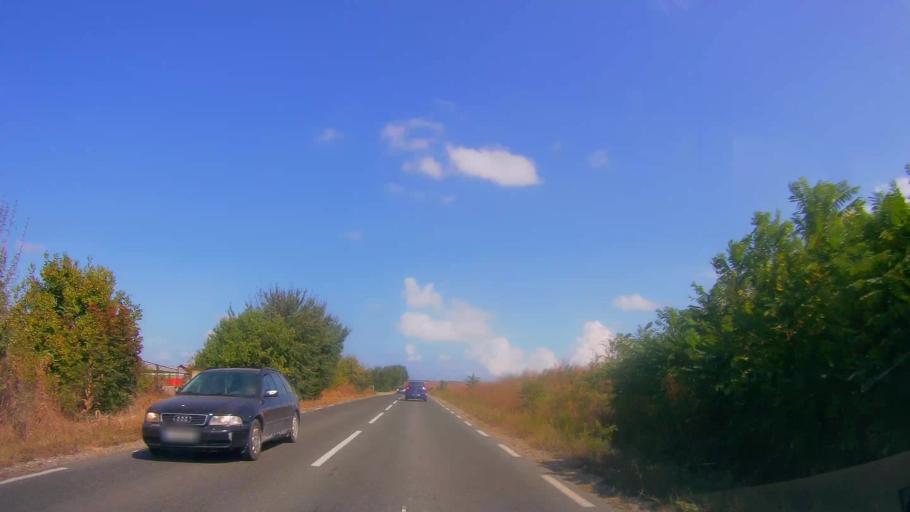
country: BG
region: Burgas
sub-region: Obshtina Burgas
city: Burgas
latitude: 42.4808
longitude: 27.3766
